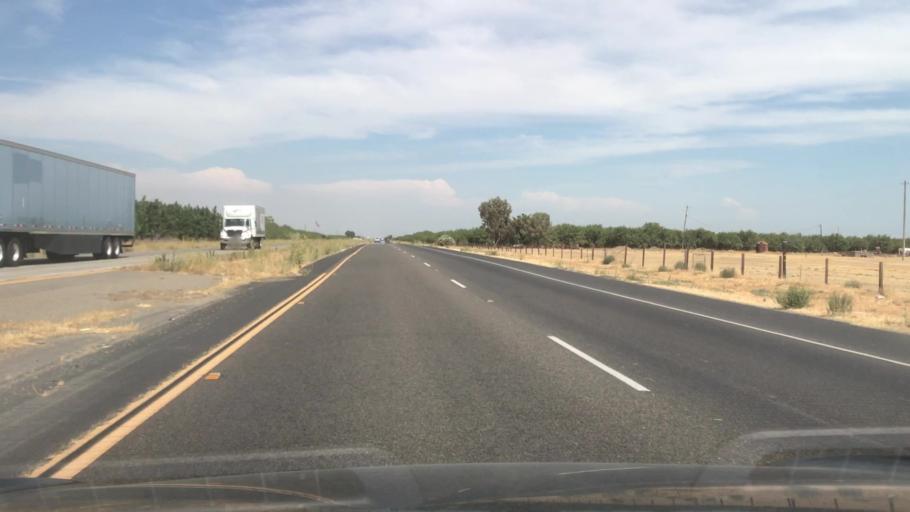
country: US
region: California
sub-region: Madera County
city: Chowchilla
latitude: 37.0835
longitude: -120.4354
